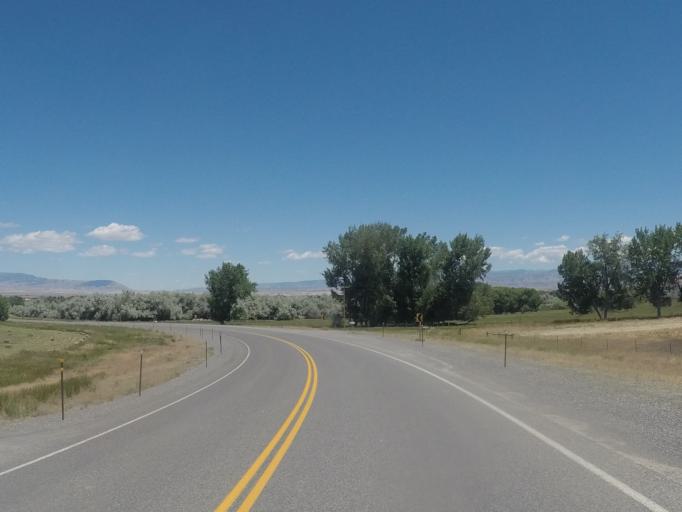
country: US
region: Wyoming
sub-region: Big Horn County
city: Lovell
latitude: 44.8005
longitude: -108.4150
